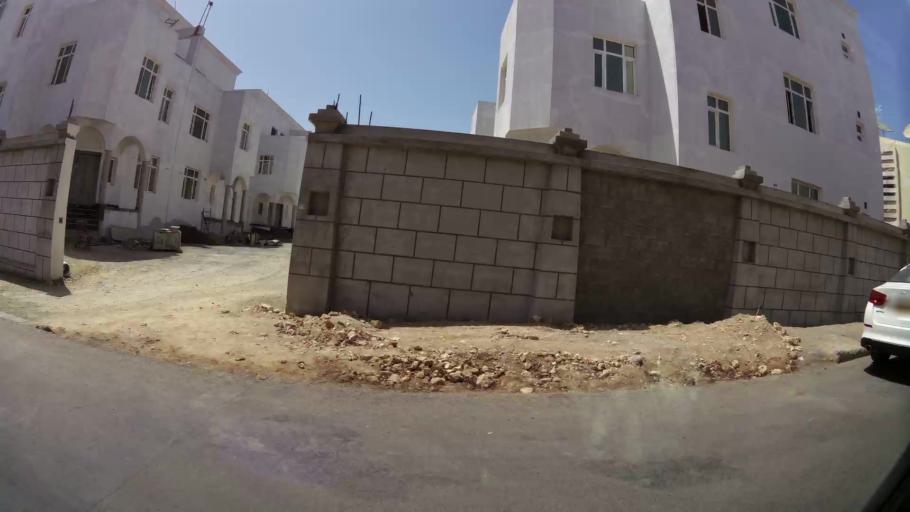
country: OM
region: Muhafazat Masqat
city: Muscat
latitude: 23.6176
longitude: 58.5059
